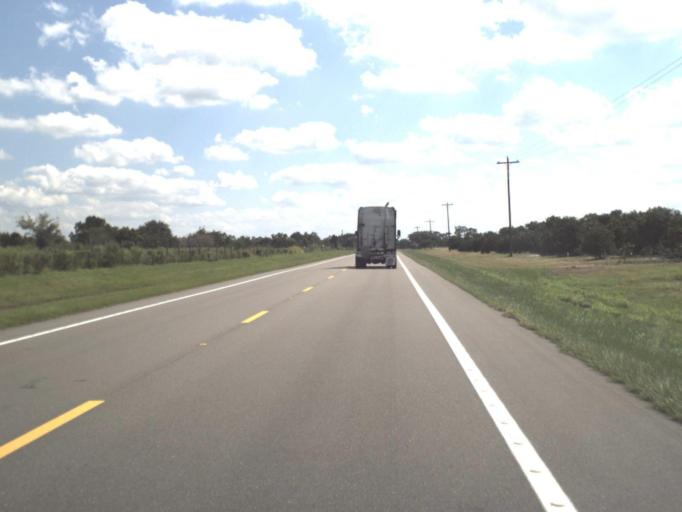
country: US
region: Florida
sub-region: Hardee County
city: Zolfo Springs
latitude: 27.4699
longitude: -81.7091
